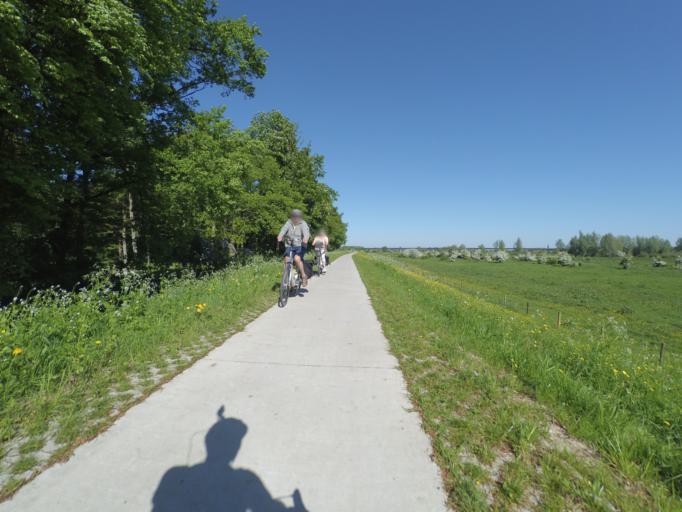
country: NL
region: Gelderland
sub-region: Gemeente Zutphen
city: Zutphen
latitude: 52.1091
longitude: 6.1943
